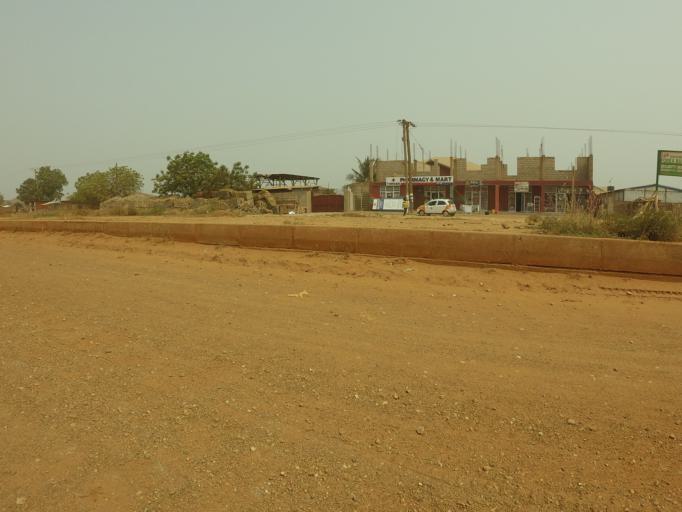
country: GH
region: Greater Accra
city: Teshi Old Town
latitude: 5.6222
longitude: -0.1247
